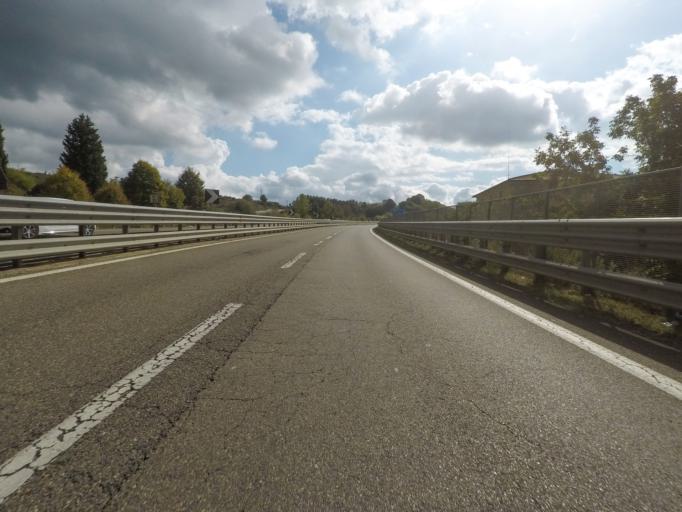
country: IT
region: Tuscany
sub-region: Provincia di Siena
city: Rapolano Terme
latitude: 43.3033
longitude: 11.5956
